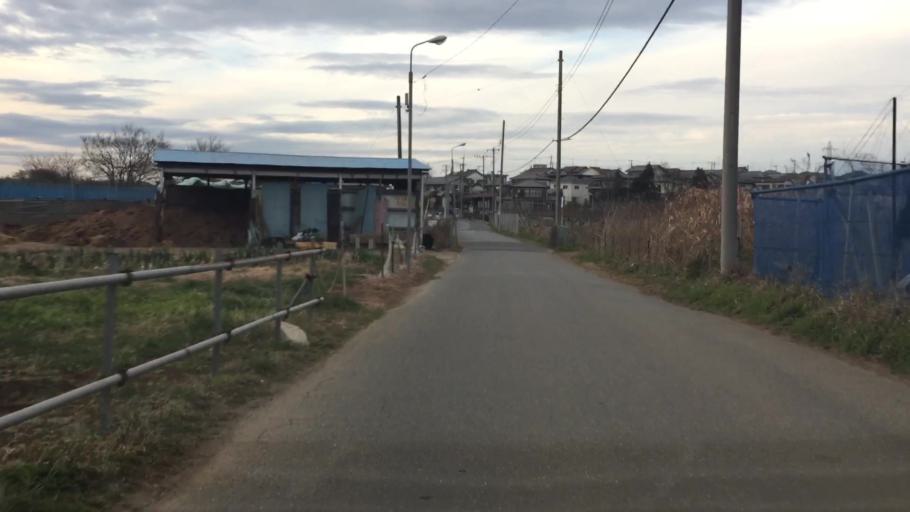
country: JP
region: Chiba
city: Shiroi
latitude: 35.7866
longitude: 139.9984
